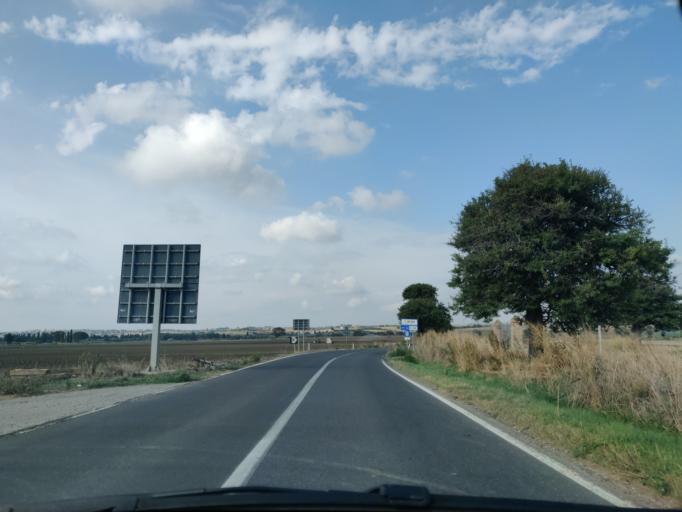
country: IT
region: Latium
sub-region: Provincia di Viterbo
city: Tarquinia
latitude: 42.2140
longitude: 11.7821
